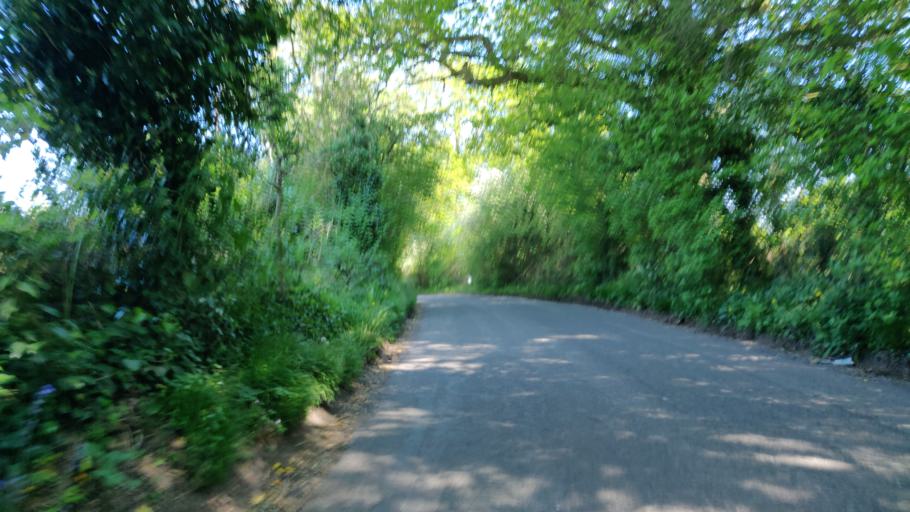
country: GB
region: England
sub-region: West Sussex
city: Billingshurst
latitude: 51.0253
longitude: -0.4123
